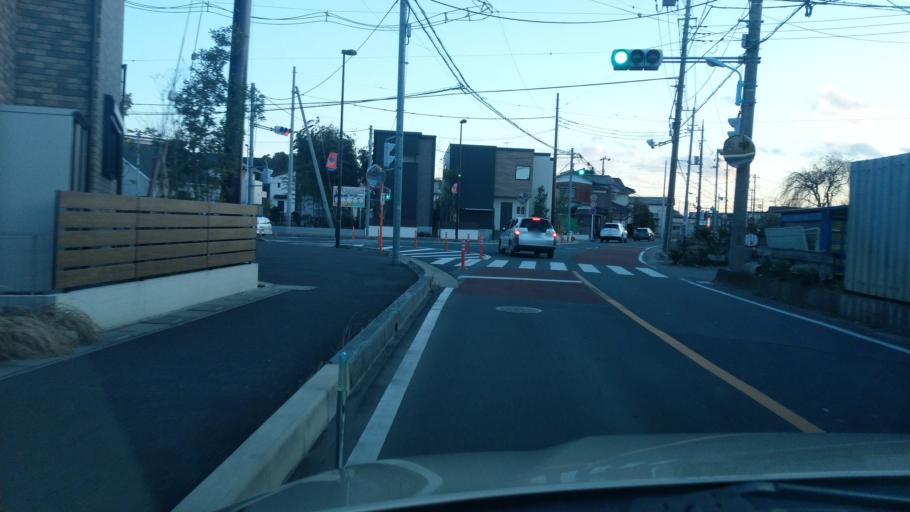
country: JP
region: Saitama
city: Ageoshimo
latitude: 35.9323
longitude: 139.5736
